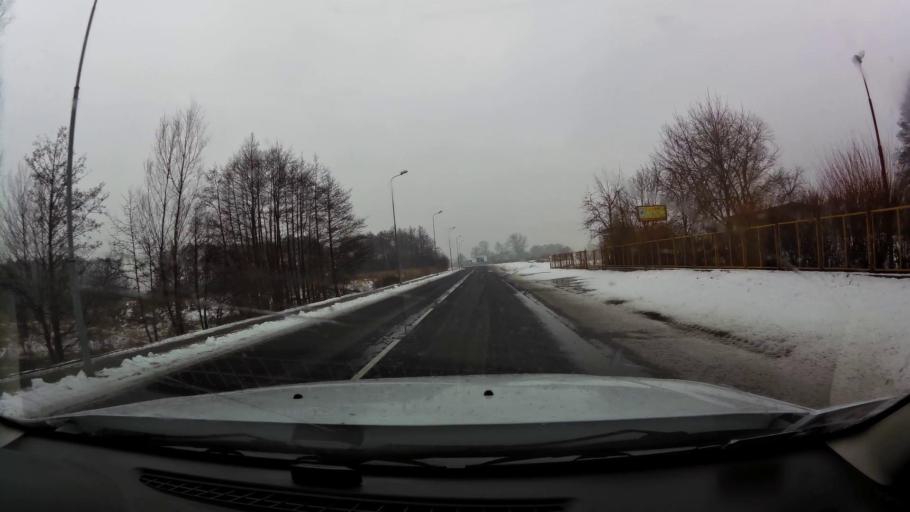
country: PL
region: West Pomeranian Voivodeship
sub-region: Powiat gryficki
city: Mrzezyno
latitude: 54.1392
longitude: 15.2865
